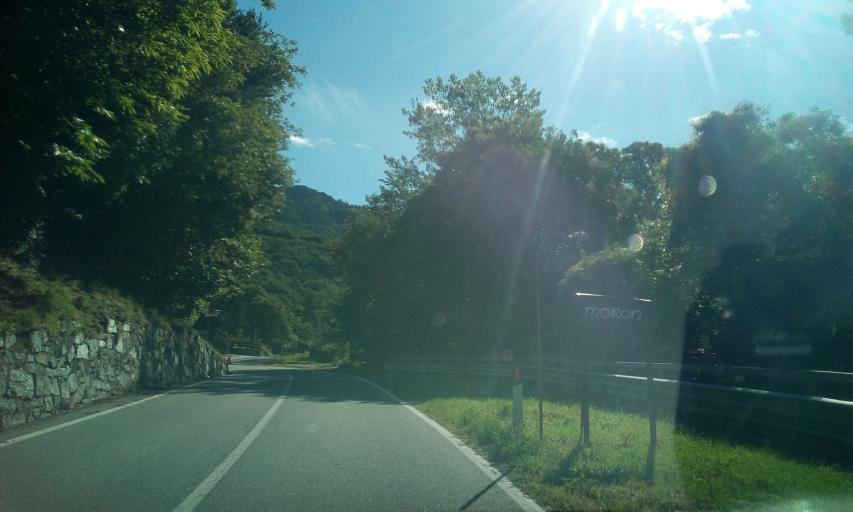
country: IT
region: Aosta Valley
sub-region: Valle d'Aosta
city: Saint-Vincent
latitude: 45.7515
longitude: 7.6593
